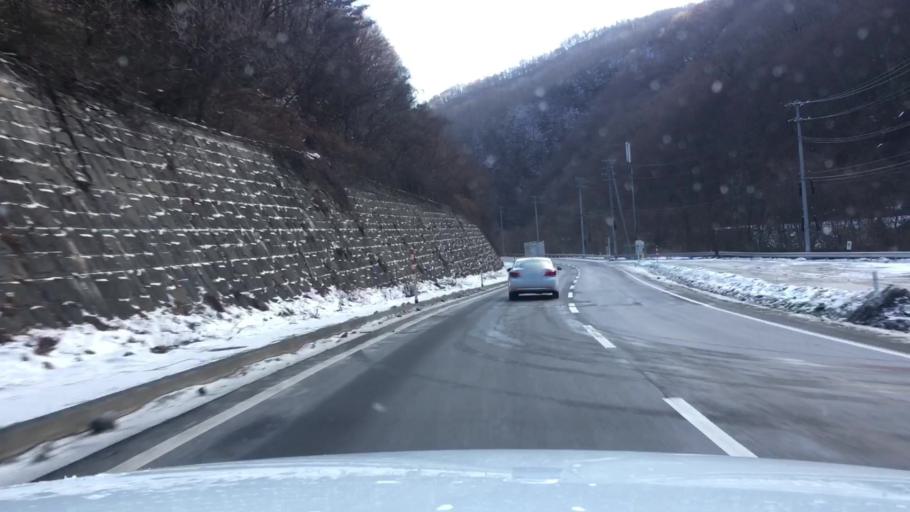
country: JP
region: Iwate
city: Tono
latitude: 39.6450
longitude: 141.5474
